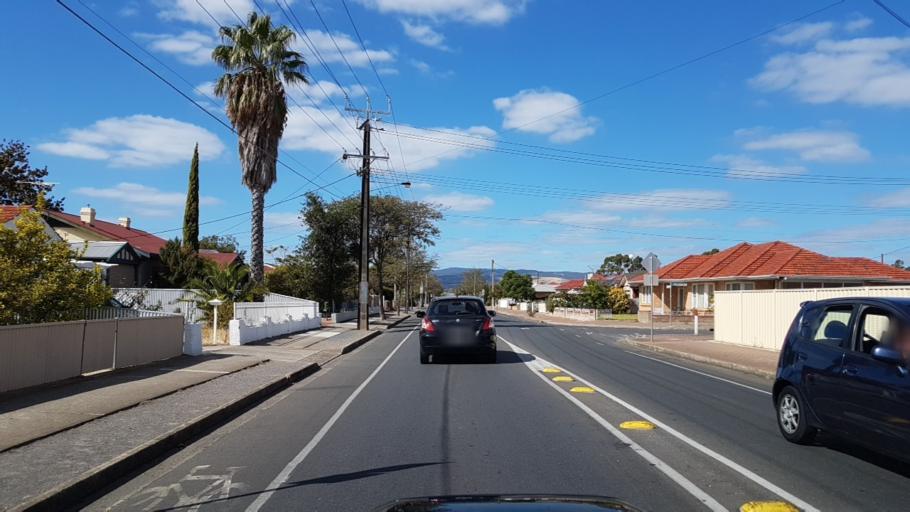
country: AU
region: South Australia
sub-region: Marion
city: Plympton Park
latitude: -34.9807
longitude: 138.5496
